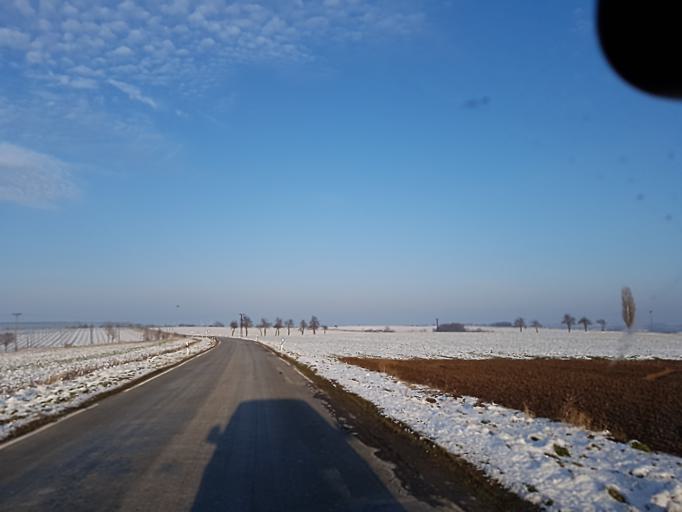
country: DE
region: Saxony
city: Grossweitzschen
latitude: 51.1966
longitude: 13.0707
